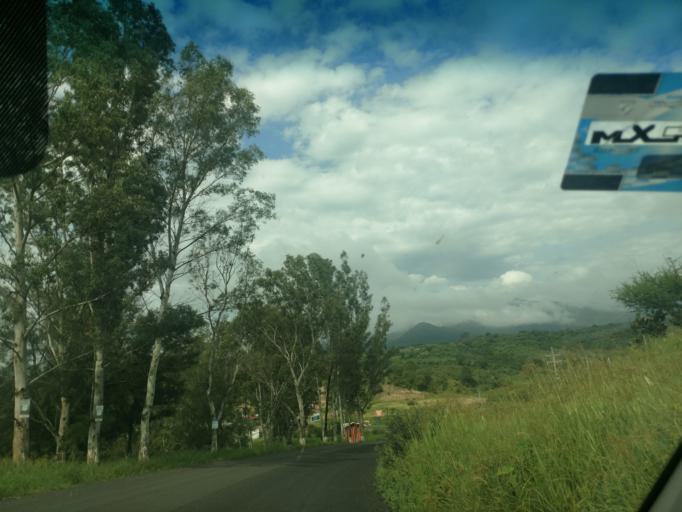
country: MX
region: Jalisco
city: El Salto
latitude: 20.4237
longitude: -104.4985
